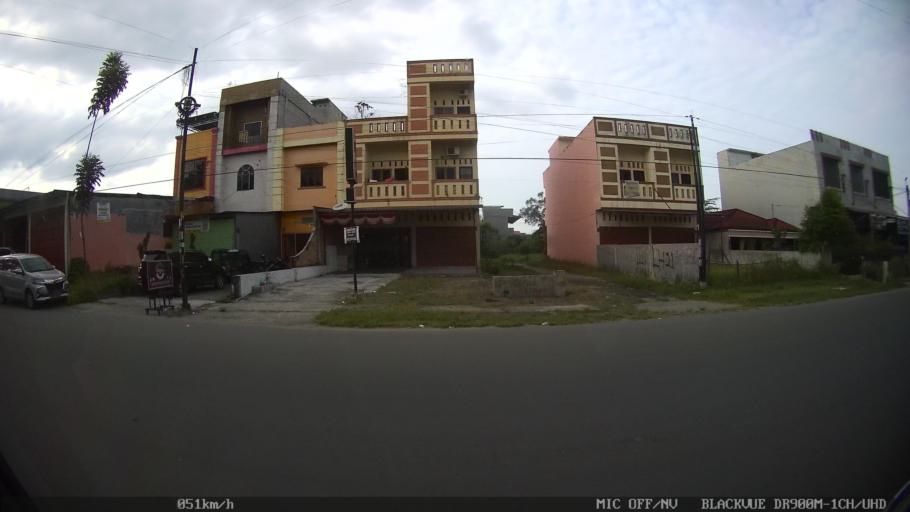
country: ID
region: North Sumatra
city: Sunggal
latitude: 3.5409
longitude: 98.6272
